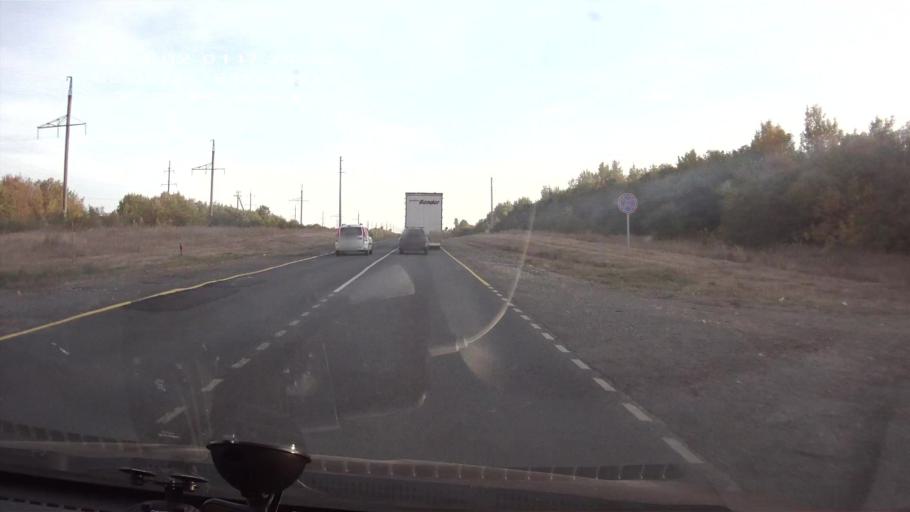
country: RU
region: Saratov
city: Krasnoarmeysk
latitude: 51.1642
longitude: 45.6491
